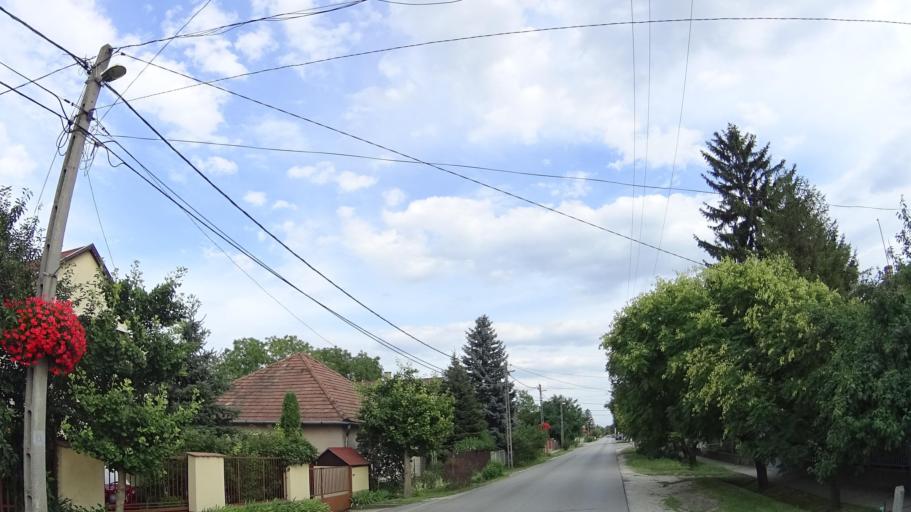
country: HU
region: Pest
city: Dunavarsany
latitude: 47.2821
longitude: 19.0587
